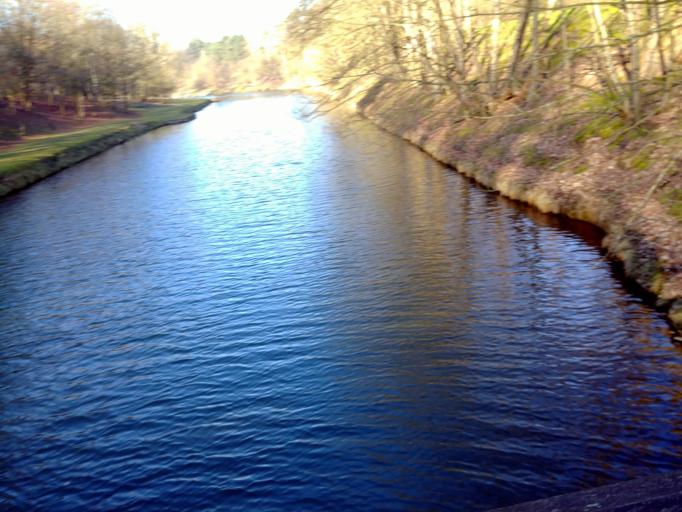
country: NL
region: North Holland
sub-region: Gemeente Bloemendaal
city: Bennebroek
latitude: 52.3473
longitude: 4.5770
